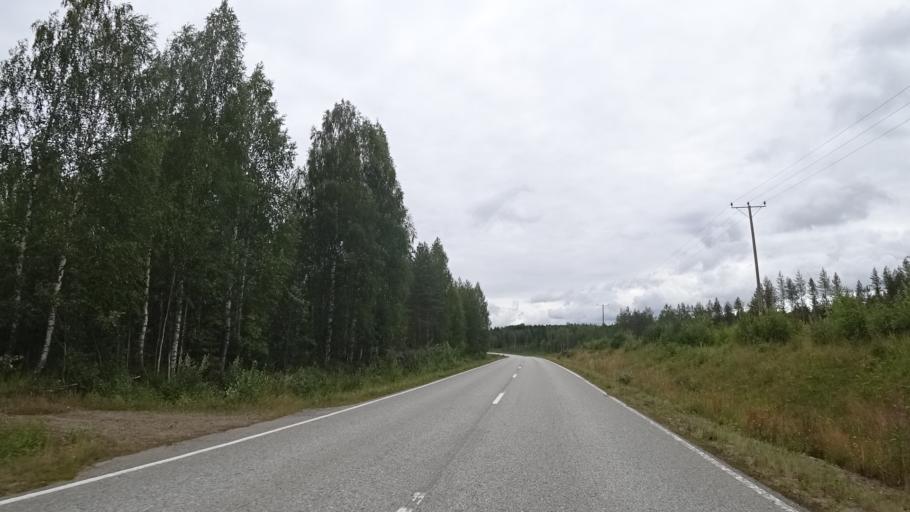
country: FI
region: North Karelia
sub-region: Joensuu
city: Ilomantsi
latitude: 62.6199
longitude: 31.2273
